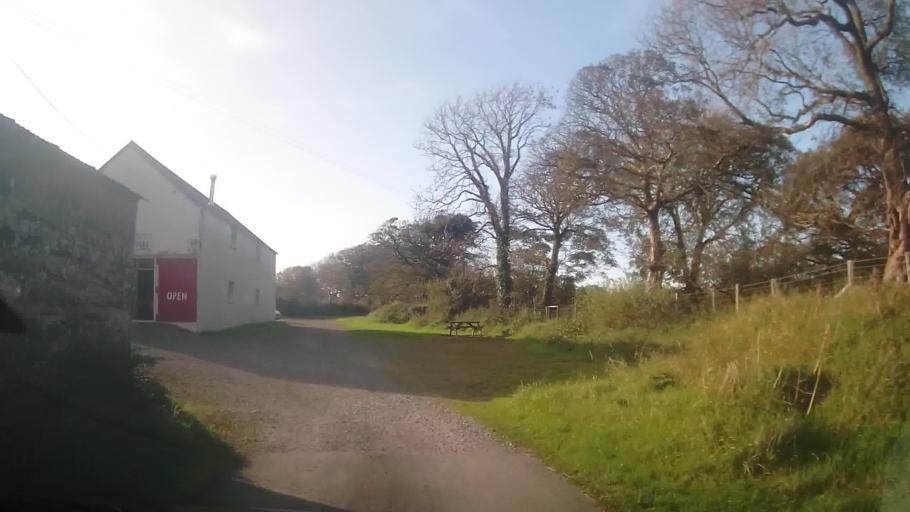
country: GB
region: Wales
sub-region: Pembrokeshire
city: Ambleston
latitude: 51.9661
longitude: -4.8944
